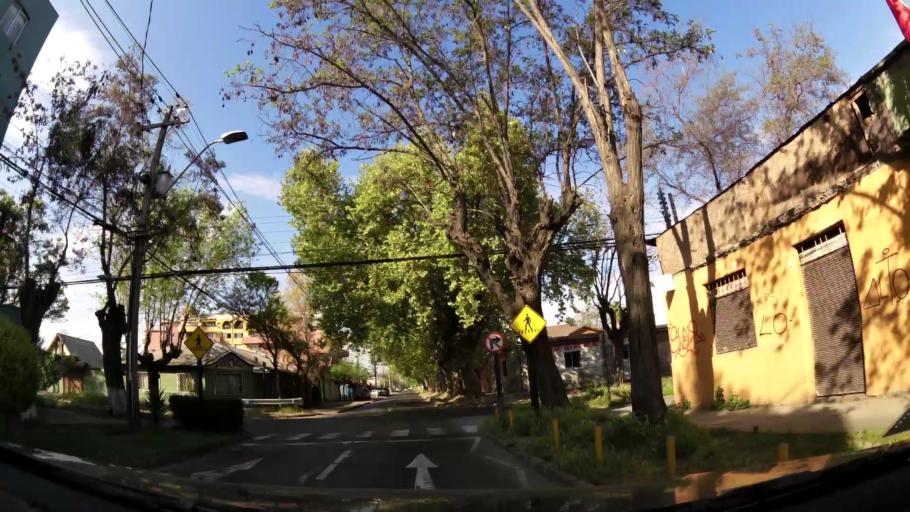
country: CL
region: Santiago Metropolitan
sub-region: Provincia de Maipo
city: San Bernardo
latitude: -33.5999
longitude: -70.7021
